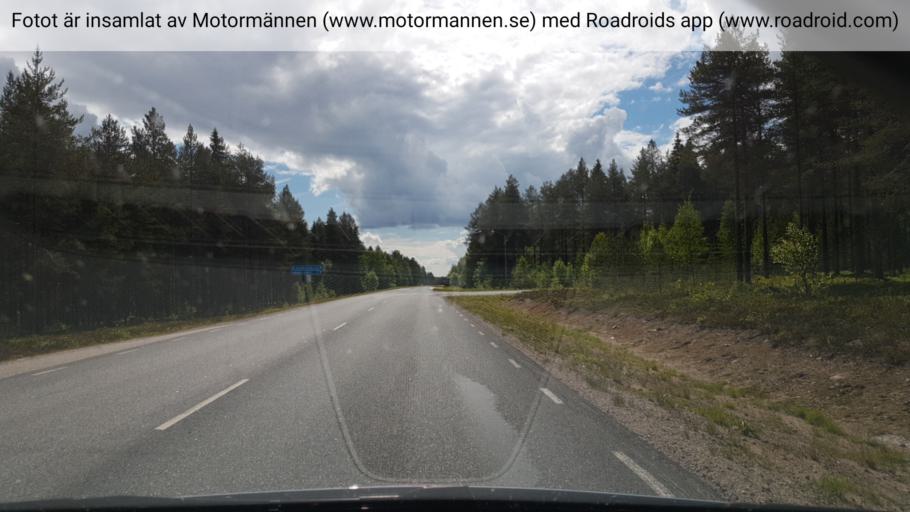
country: FI
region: Lapland
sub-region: Torniolaakso
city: Ylitornio
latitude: 66.2956
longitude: 23.6373
